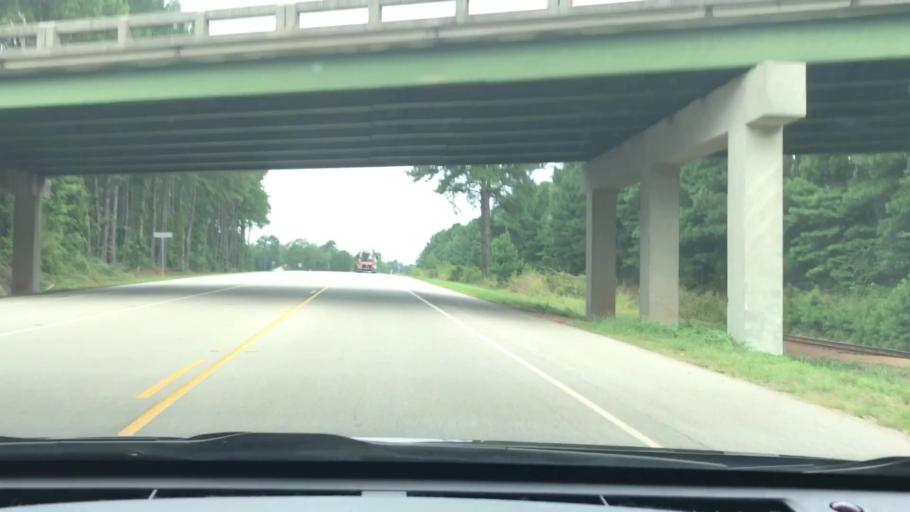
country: US
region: Georgia
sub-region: Taliaferro County
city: Crawfordville
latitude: 33.4989
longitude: -82.8041
